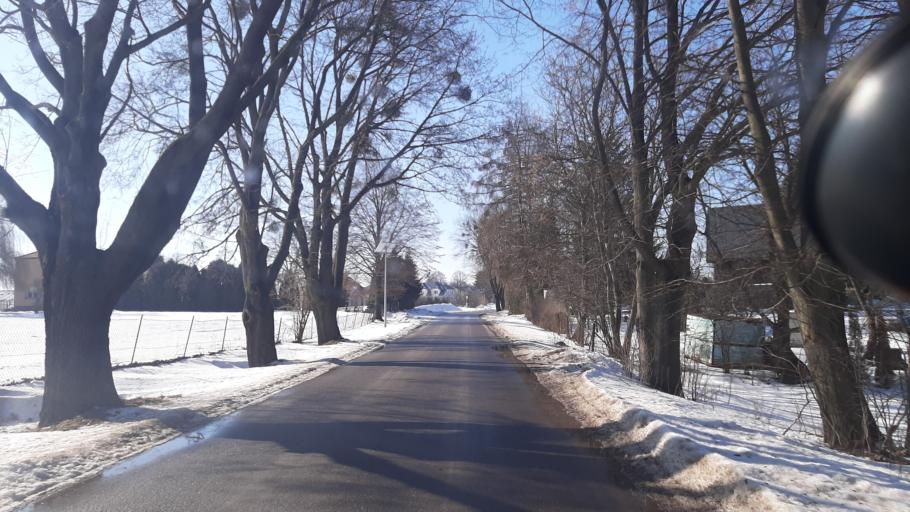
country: PL
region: Lublin Voivodeship
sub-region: Powiat pulawski
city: Naleczow
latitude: 51.2971
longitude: 22.2350
